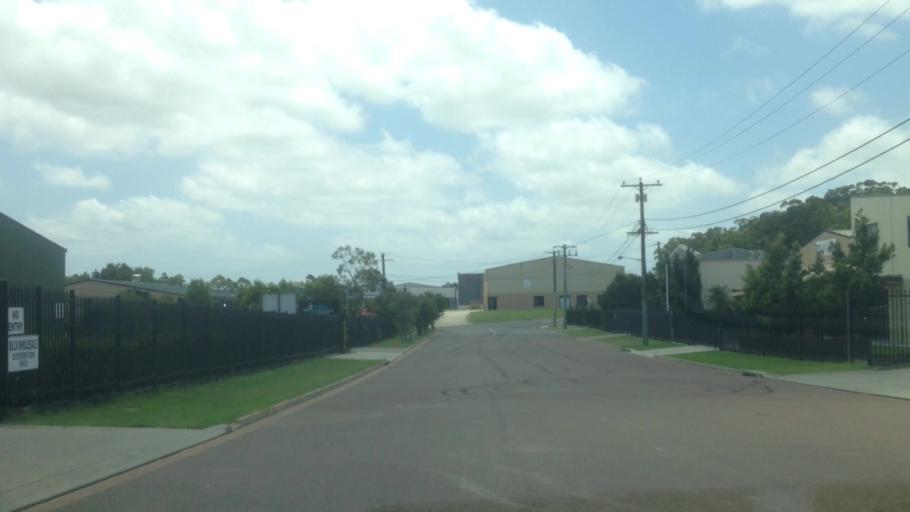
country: AU
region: New South Wales
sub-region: Lake Macquarie Shire
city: Dora Creek
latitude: -33.1191
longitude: 151.4733
